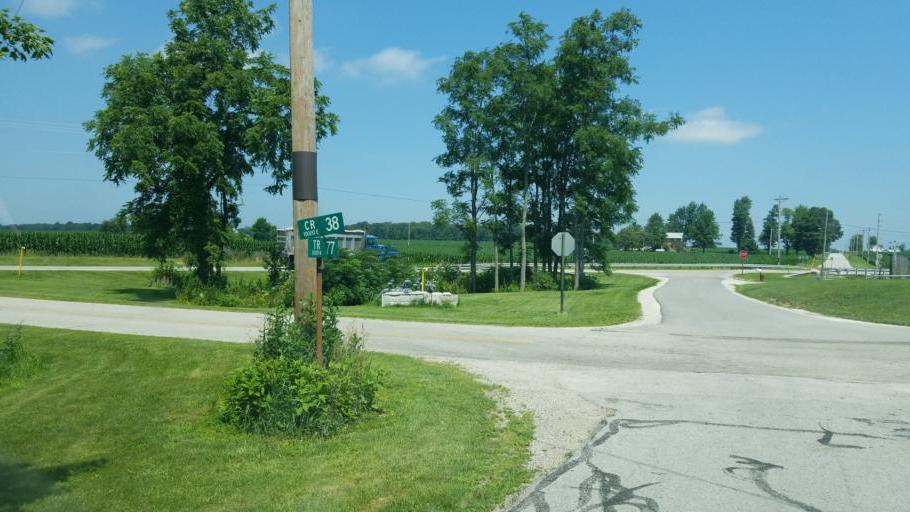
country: US
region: Ohio
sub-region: Sandusky County
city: Mount Carmel
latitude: 41.1692
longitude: -82.9764
